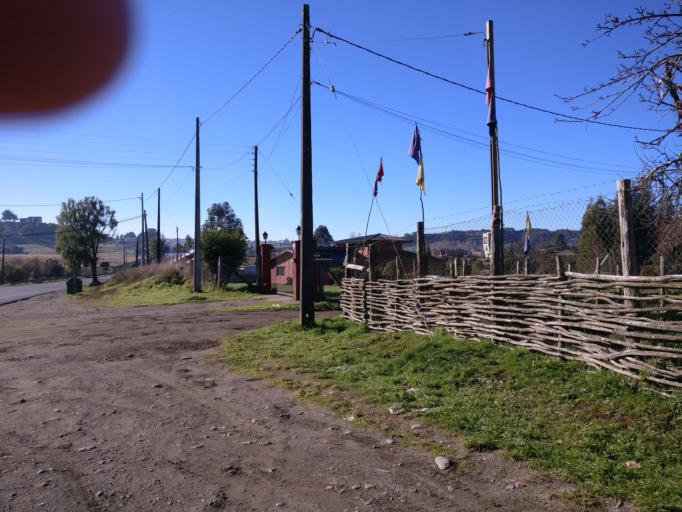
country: CL
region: Los Lagos
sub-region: Provincia de Chiloe
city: Castro
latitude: -42.4218
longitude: -73.7448
